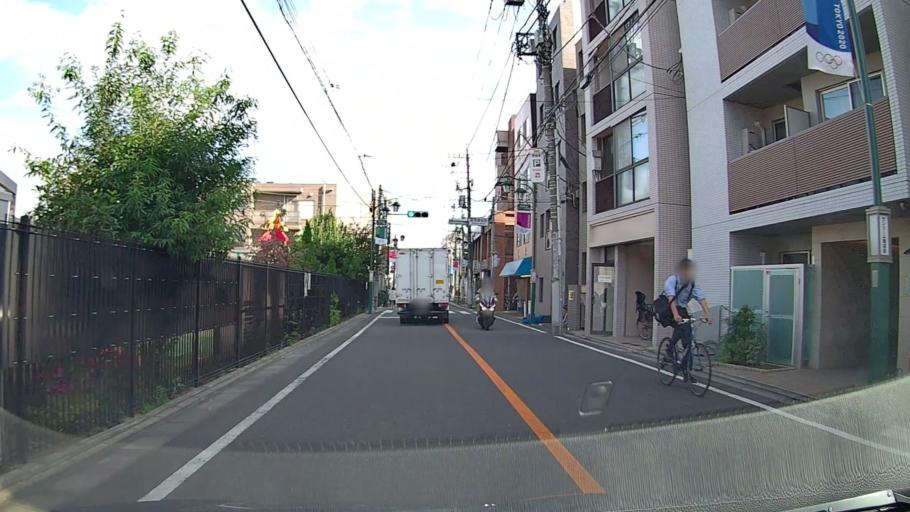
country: JP
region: Saitama
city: Wako
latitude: 35.7489
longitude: 139.6420
